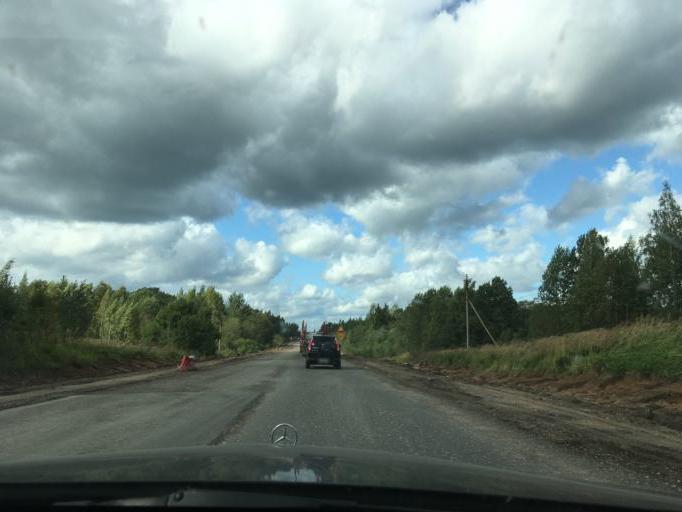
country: RU
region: Pskov
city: Novosokol'niki
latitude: 56.2918
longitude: 30.2426
